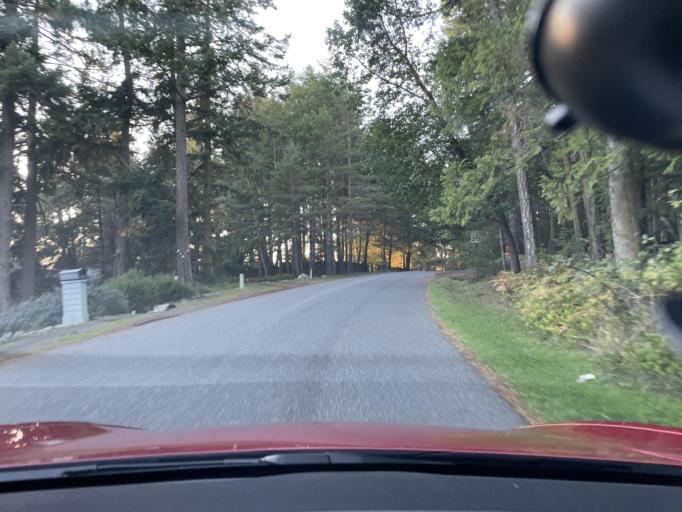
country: US
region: Washington
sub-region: San Juan County
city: Friday Harbor
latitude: 48.6130
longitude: -123.1526
